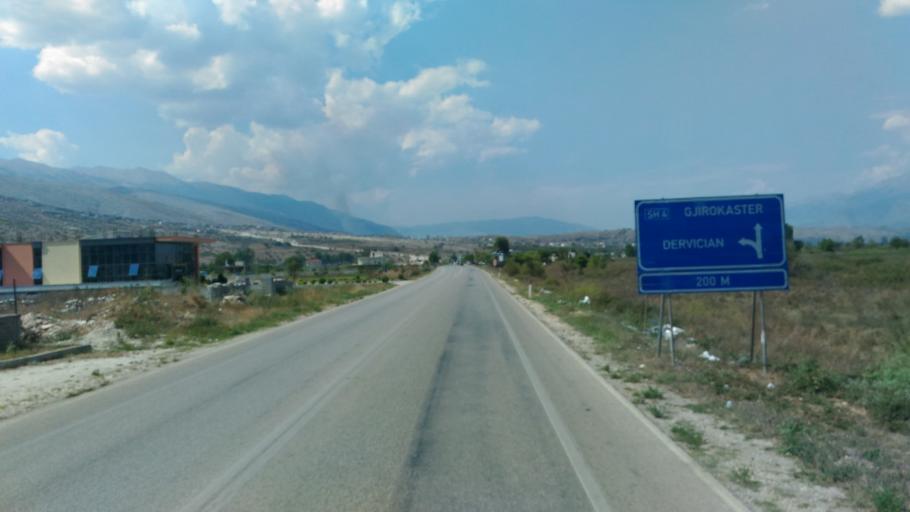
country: AL
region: Gjirokaster
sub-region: Rrethi i Gjirokastres
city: Dervician
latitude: 40.0315
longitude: 20.1843
